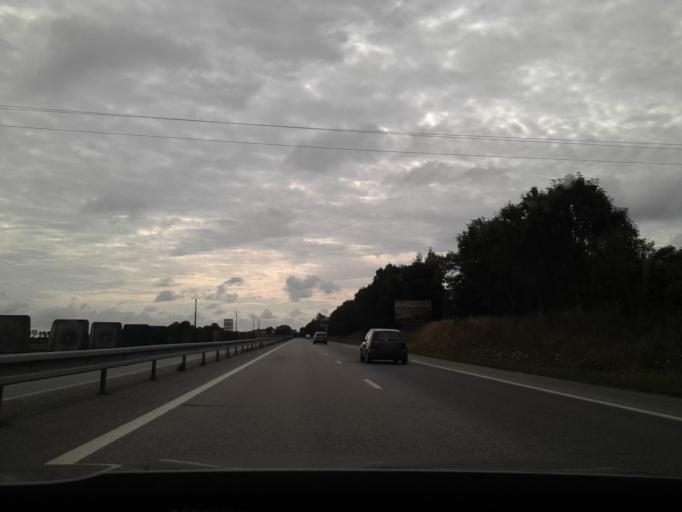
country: FR
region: Lower Normandy
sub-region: Departement de la Manche
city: Saint-Hilaire-Petitville
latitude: 49.3038
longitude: -1.1955
